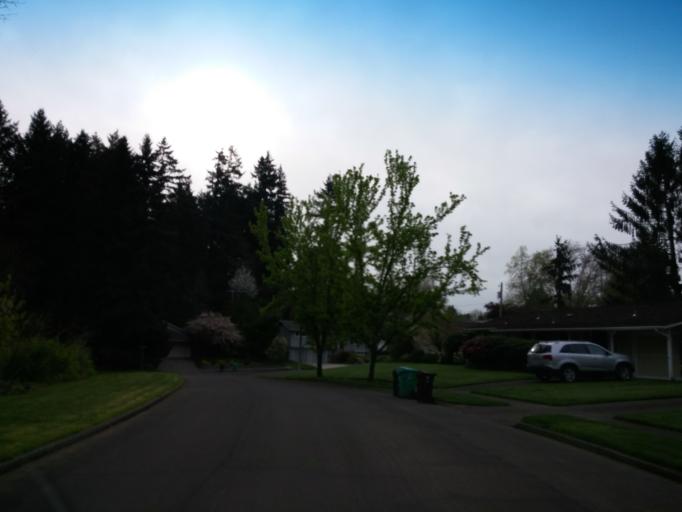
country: US
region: Oregon
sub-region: Washington County
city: Cedar Hills
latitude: 45.5115
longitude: -122.8033
